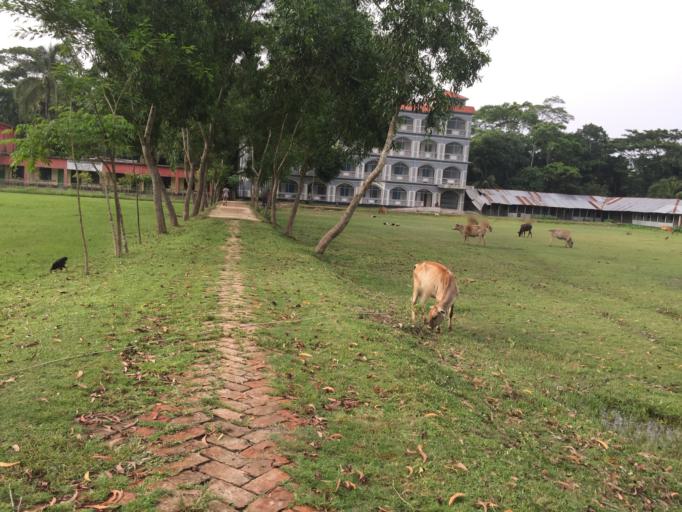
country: BD
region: Barisal
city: Mathba
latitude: 22.1895
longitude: 89.9257
